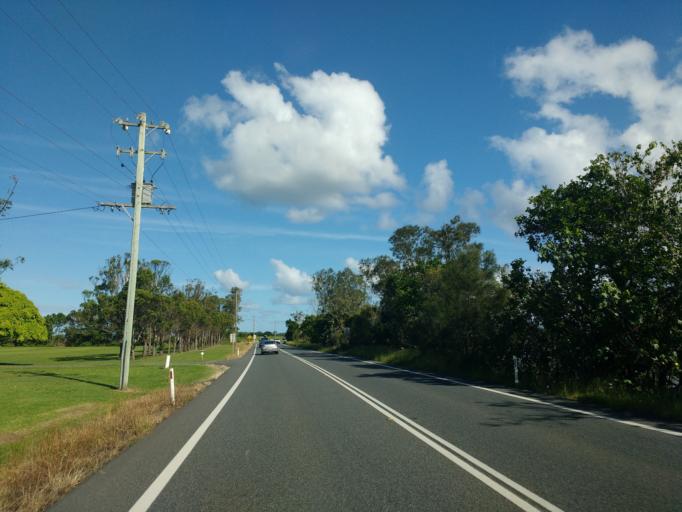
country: AU
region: New South Wales
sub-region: Richmond Valley
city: Evans Head
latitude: -28.9860
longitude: 153.4621
